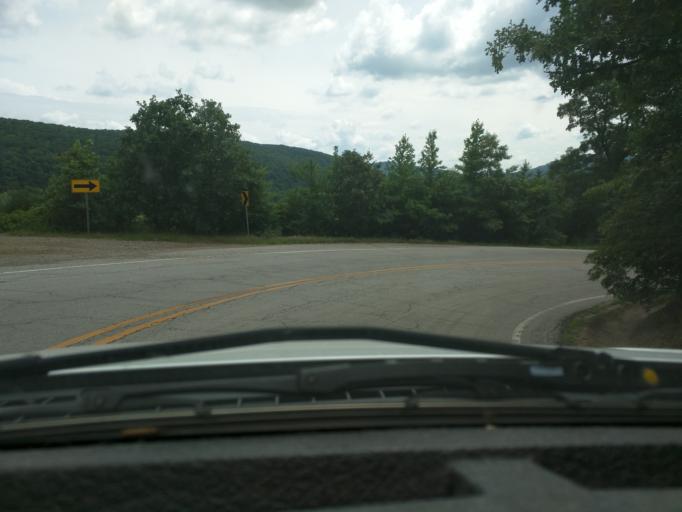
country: US
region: Arkansas
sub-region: Franklin County
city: Ozark
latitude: 35.6928
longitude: -93.8116
